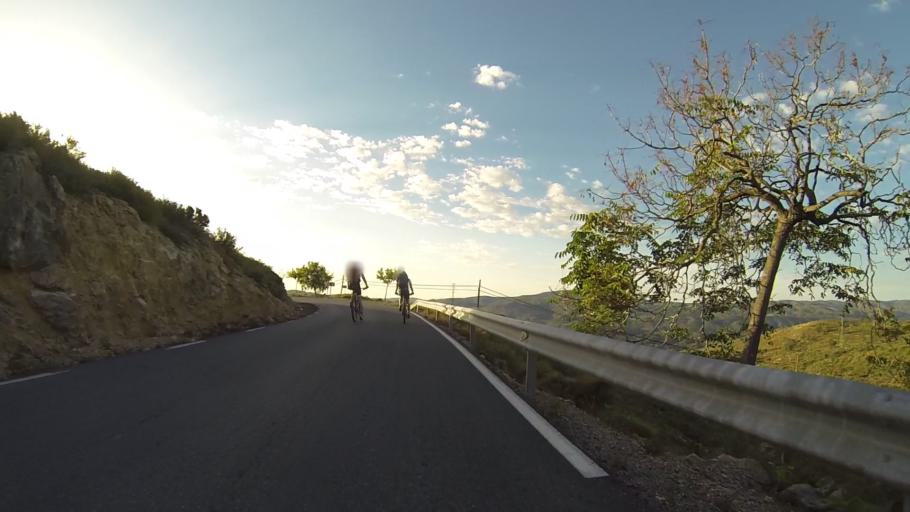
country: ES
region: Andalusia
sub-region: Provincia de Granada
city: Valor
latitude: 36.9785
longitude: -3.1291
